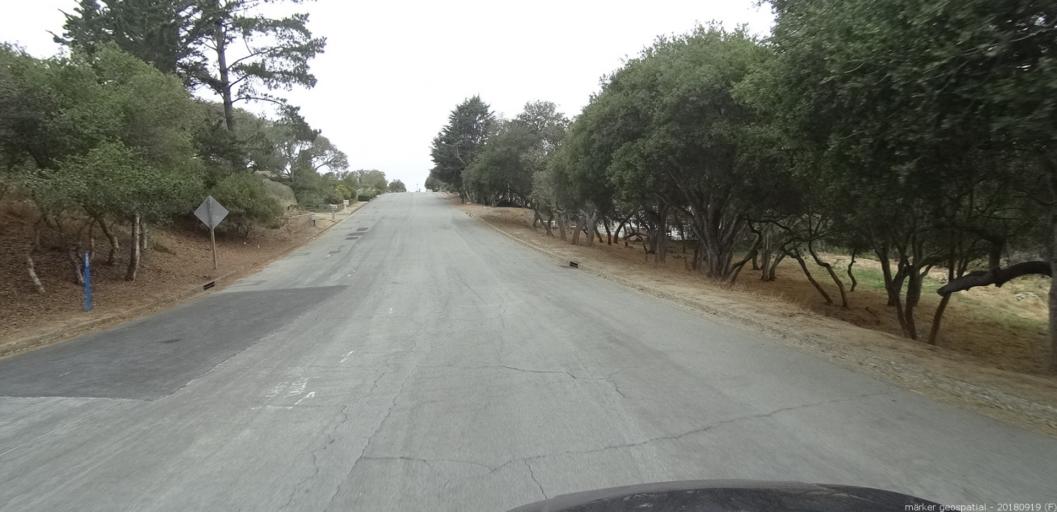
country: US
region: California
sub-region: Monterey County
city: Prunedale
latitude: 36.7816
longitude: -121.7044
